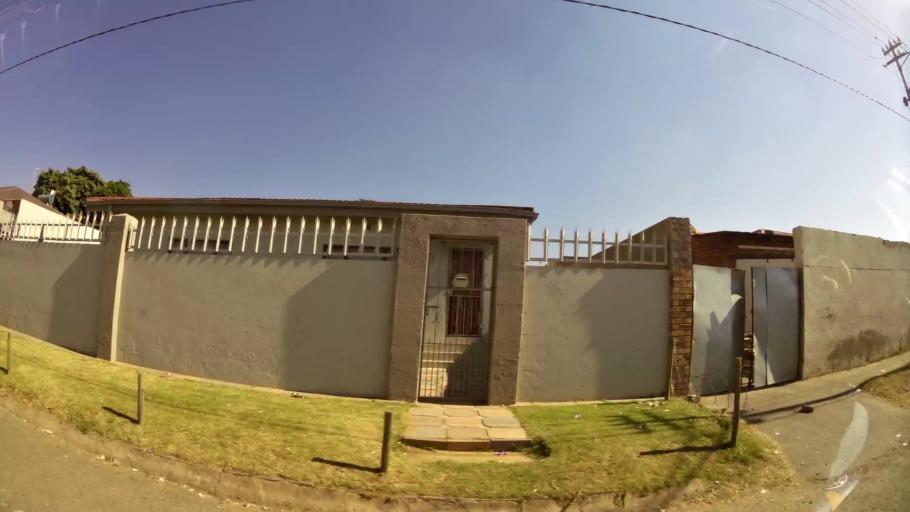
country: ZA
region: Gauteng
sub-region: City of Johannesburg Metropolitan Municipality
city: Johannesburg
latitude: -26.1800
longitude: 27.9638
